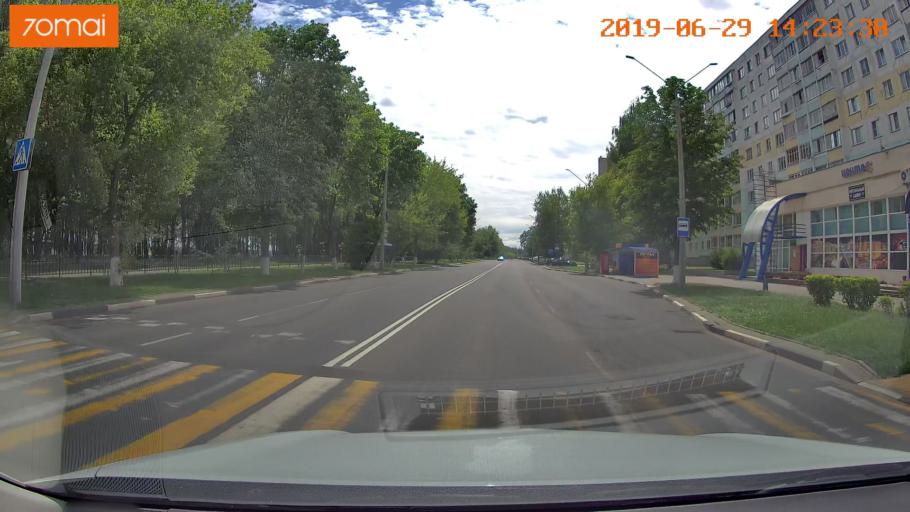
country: BY
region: Minsk
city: Salihorsk
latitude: 52.7855
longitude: 27.5541
